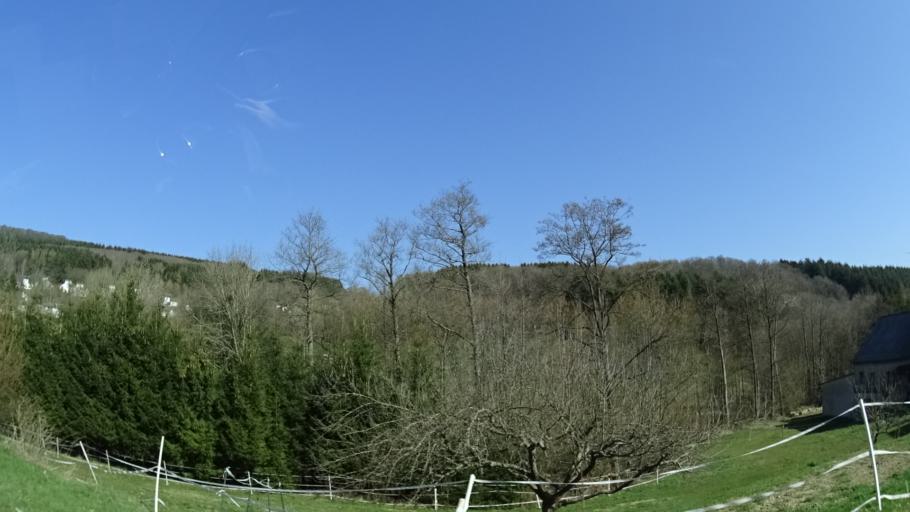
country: DE
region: Rheinland-Pfalz
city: Oberhambach
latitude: 49.6863
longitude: 7.1546
